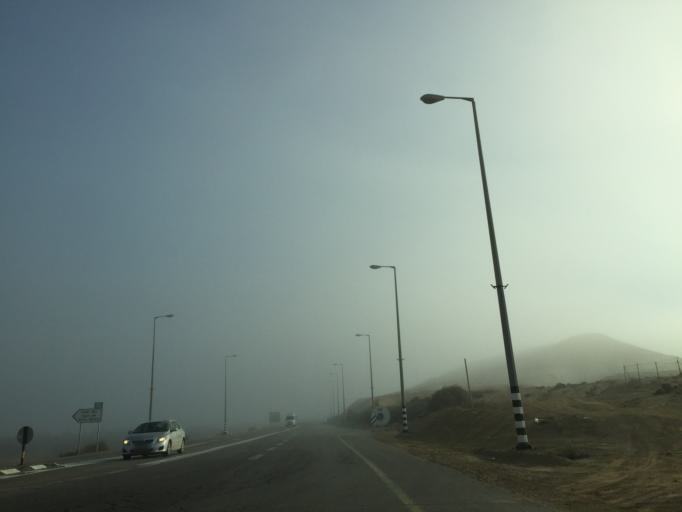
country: IL
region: Southern District
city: Yeroham
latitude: 30.9933
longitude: 34.9165
